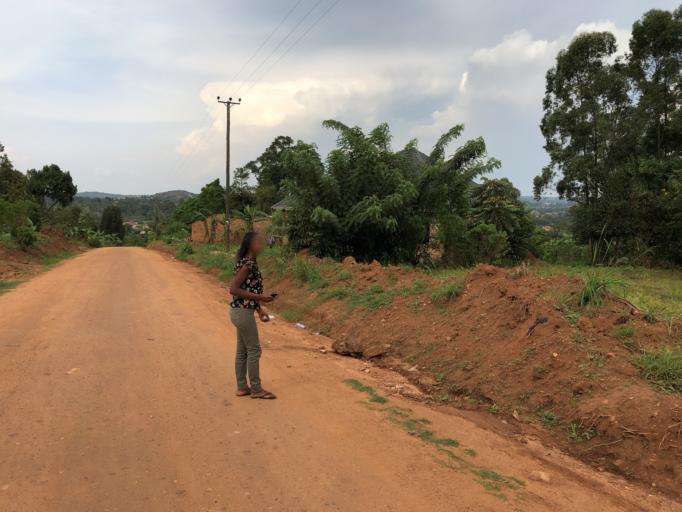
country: UG
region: Central Region
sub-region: Wakiso District
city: Bweyogerere
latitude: 0.4788
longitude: 32.6401
